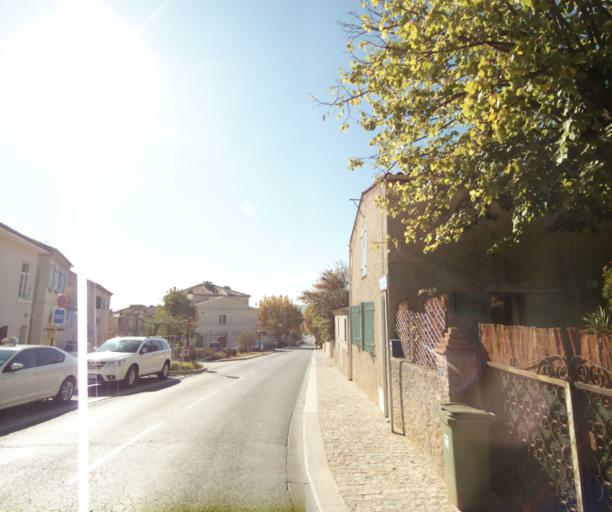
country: FR
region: Provence-Alpes-Cote d'Azur
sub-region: Departement des Bouches-du-Rhone
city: Ceyreste
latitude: 43.2149
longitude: 5.6323
